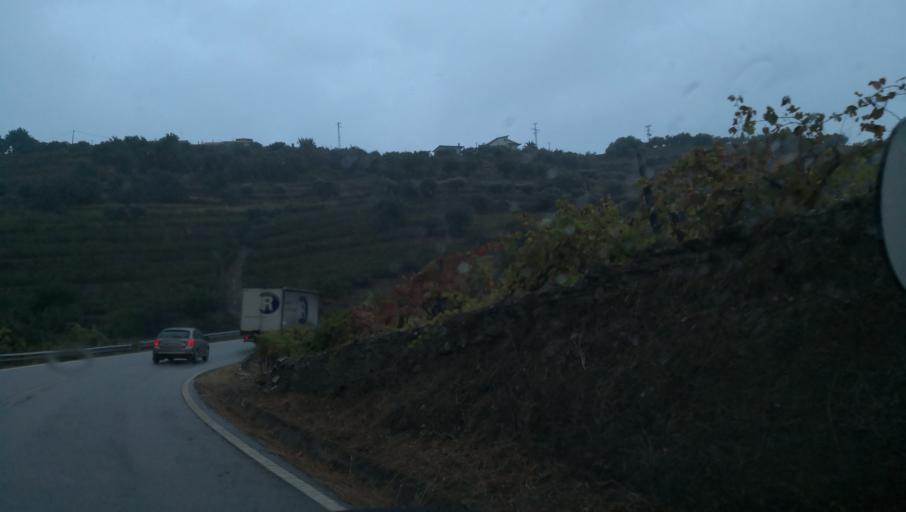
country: PT
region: Vila Real
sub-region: Santa Marta de Penaguiao
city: Santa Marta de Penaguiao
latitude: 41.2234
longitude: -7.7313
